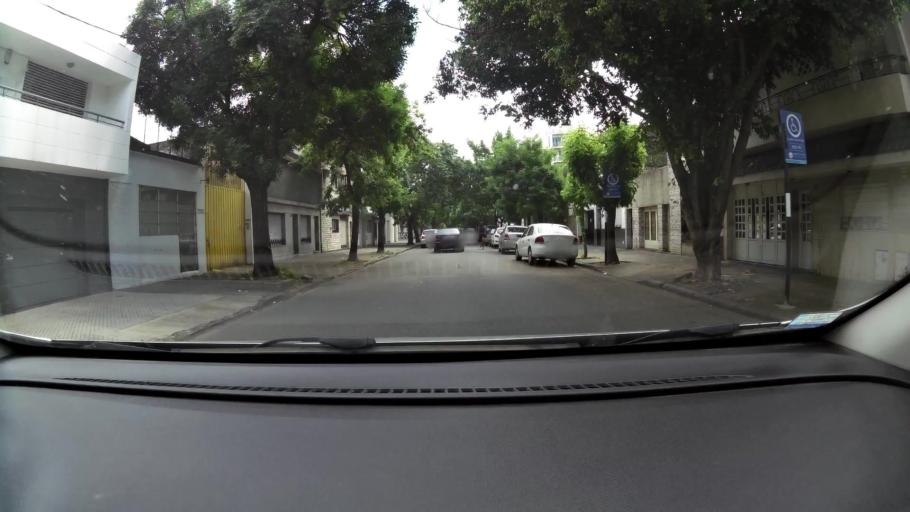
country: AR
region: Santa Fe
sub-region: Departamento de Rosario
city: Rosario
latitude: -32.9668
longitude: -60.6447
